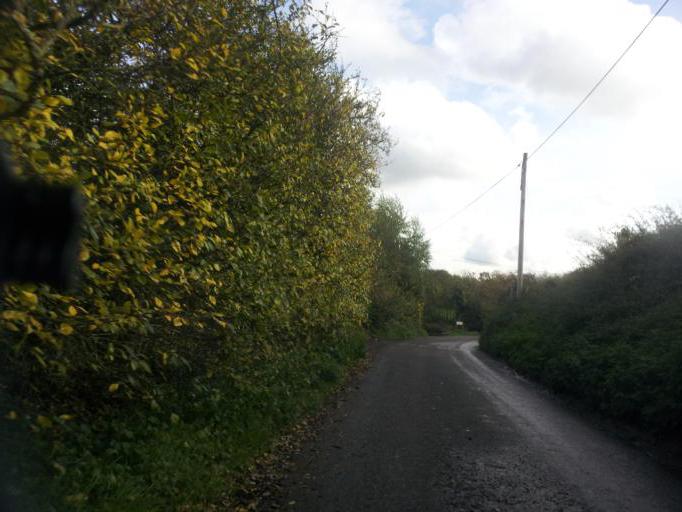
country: GB
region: England
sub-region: Kent
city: Newington
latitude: 51.3588
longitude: 0.6684
